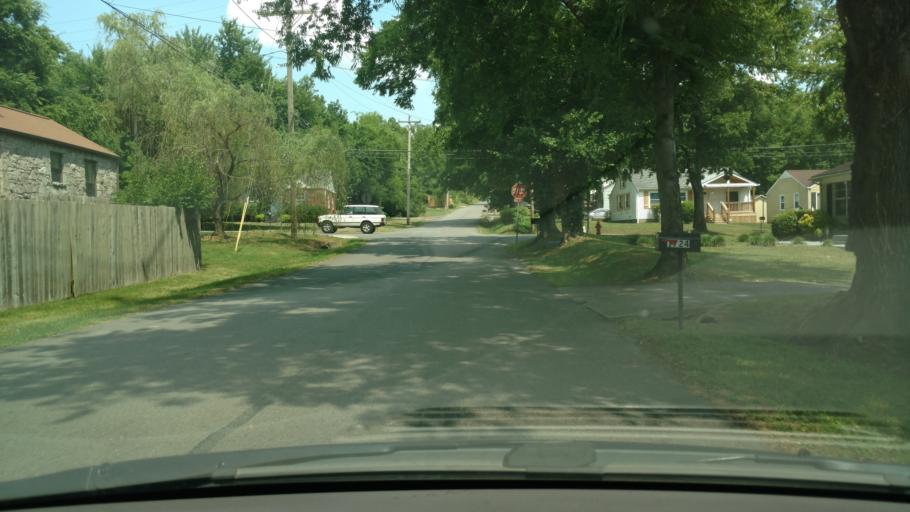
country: US
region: Tennessee
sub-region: Davidson County
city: Nashville
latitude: 36.1926
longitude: -86.7336
